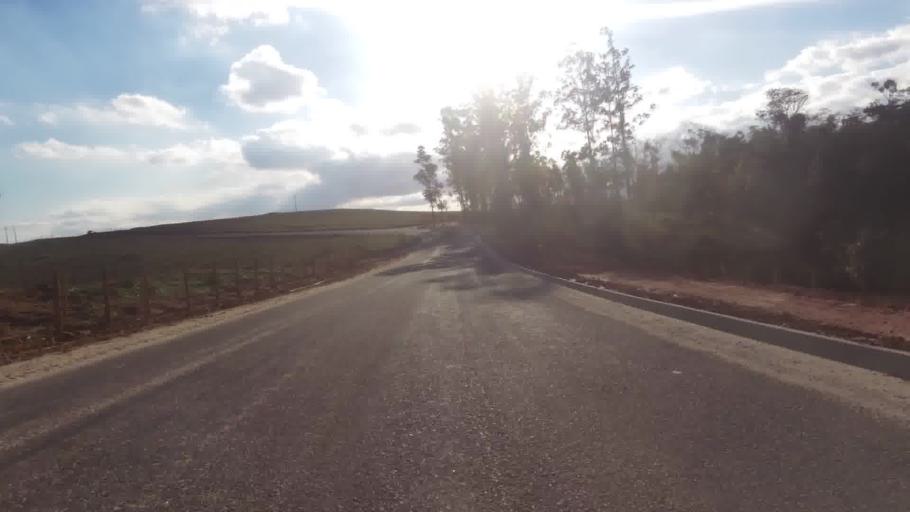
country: BR
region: Espirito Santo
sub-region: Marataizes
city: Marataizes
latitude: -21.1419
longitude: -41.0610
